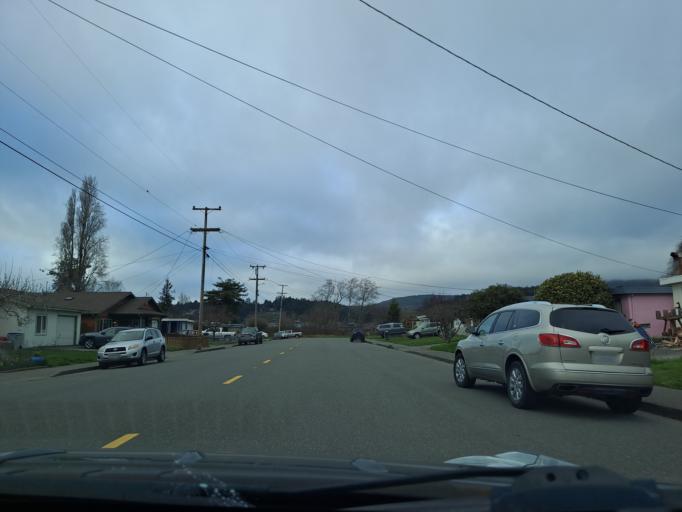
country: US
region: California
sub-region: Humboldt County
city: Fortuna
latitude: 40.5898
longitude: -124.1524
